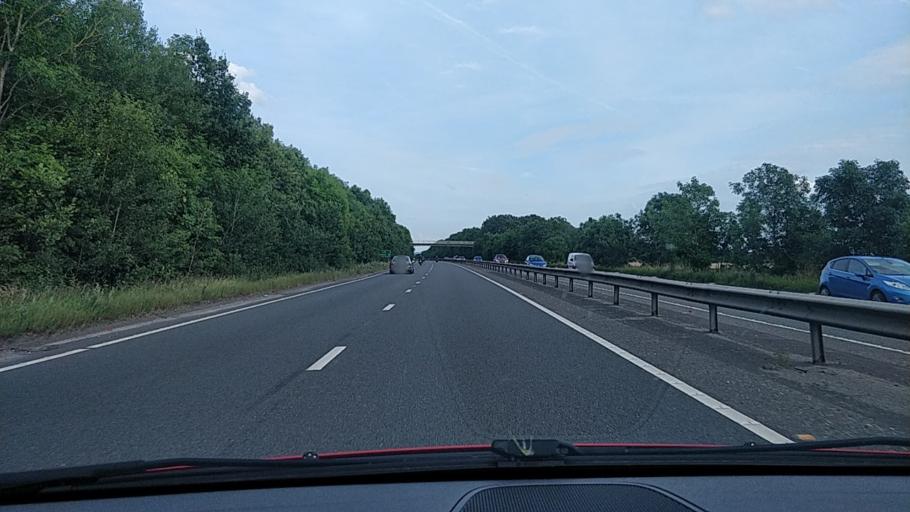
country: GB
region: Wales
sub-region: Wrexham
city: Rossett
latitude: 53.1619
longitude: -2.9624
